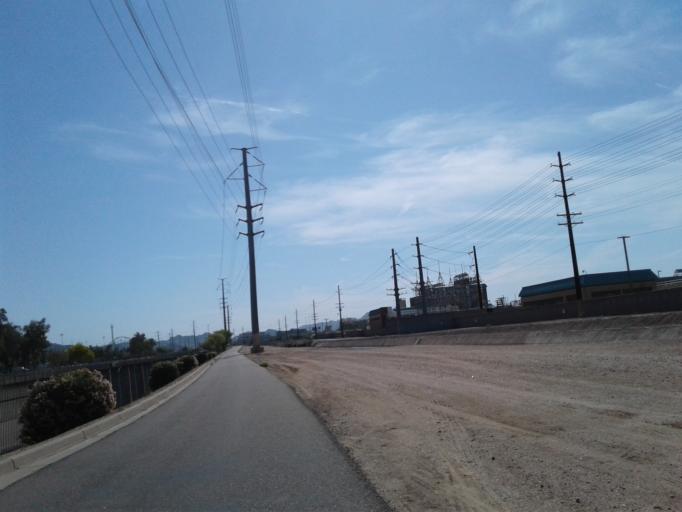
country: US
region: Arizona
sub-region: Maricopa County
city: Glendale
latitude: 33.5704
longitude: -112.1281
